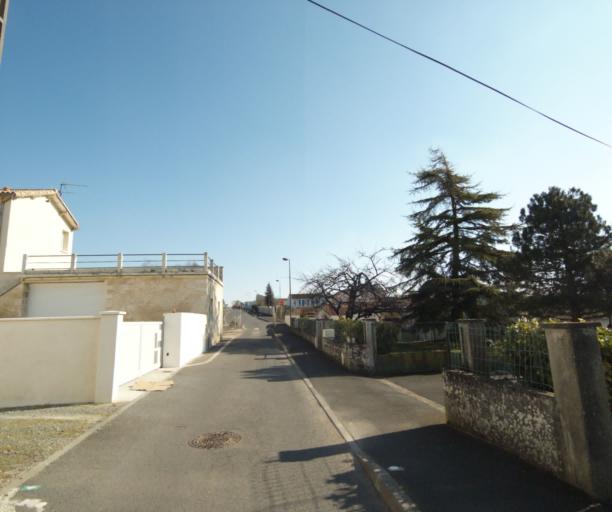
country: FR
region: Poitou-Charentes
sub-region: Departement des Deux-Sevres
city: Aiffres
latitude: 46.3302
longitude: -0.4226
